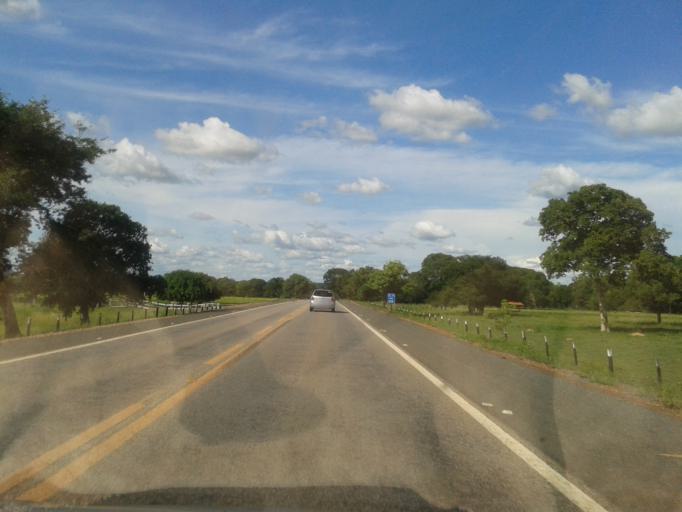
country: BR
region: Goias
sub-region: Mozarlandia
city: Mozarlandia
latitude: -15.0087
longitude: -50.5923
